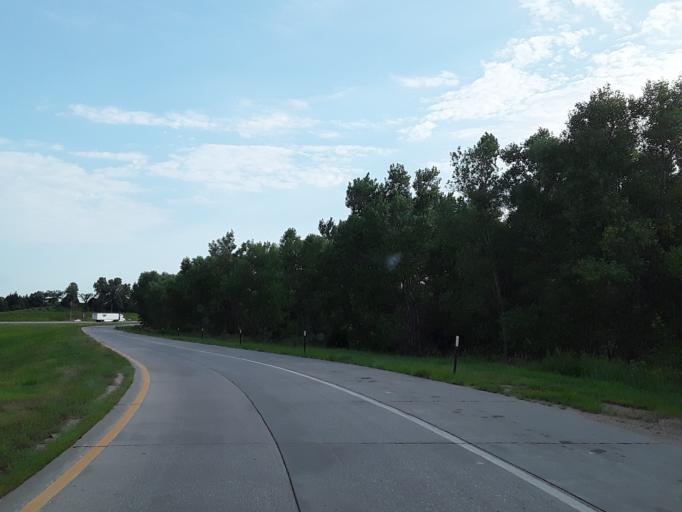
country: US
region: Nebraska
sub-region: Saunders County
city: Ashland
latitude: 41.0125
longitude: -96.3102
